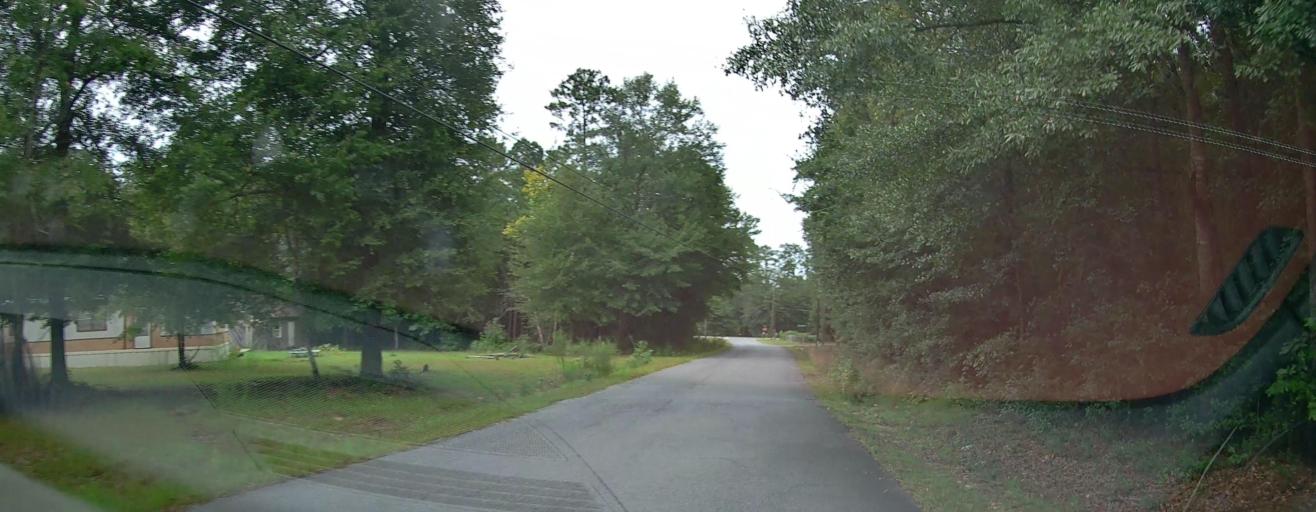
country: US
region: Georgia
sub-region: Peach County
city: Byron
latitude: 32.6781
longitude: -83.7140
